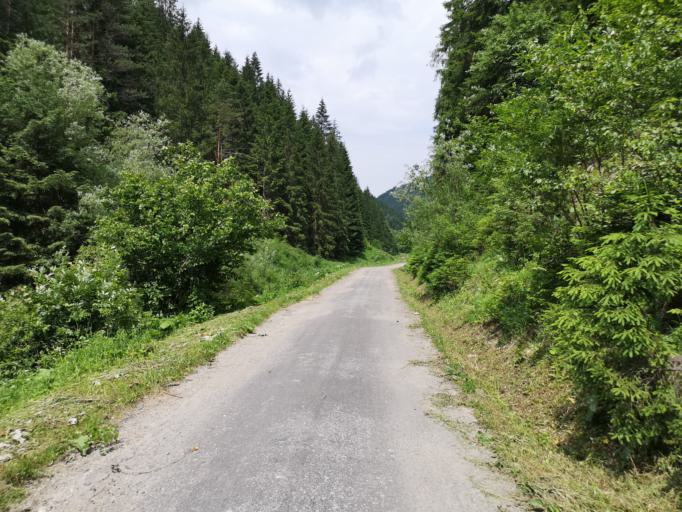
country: SK
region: Zilinsky
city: Ruzomberok
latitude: 49.1382
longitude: 19.4191
